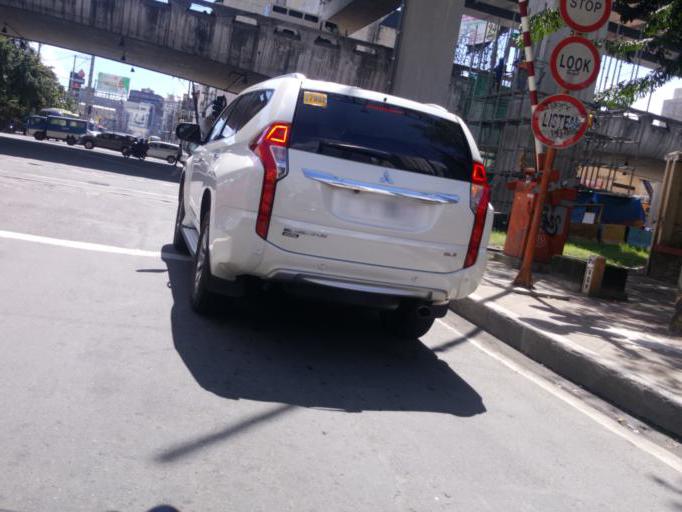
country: PH
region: Metro Manila
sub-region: Makati City
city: Makati City
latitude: 14.5586
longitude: 121.0074
